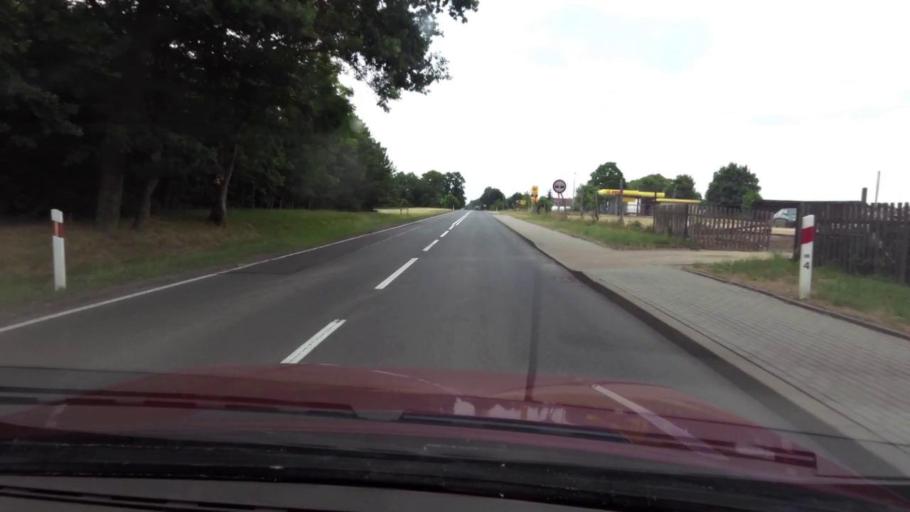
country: PL
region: Pomeranian Voivodeship
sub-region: Powiat bytowski
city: Trzebielino
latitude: 54.2090
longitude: 17.0898
